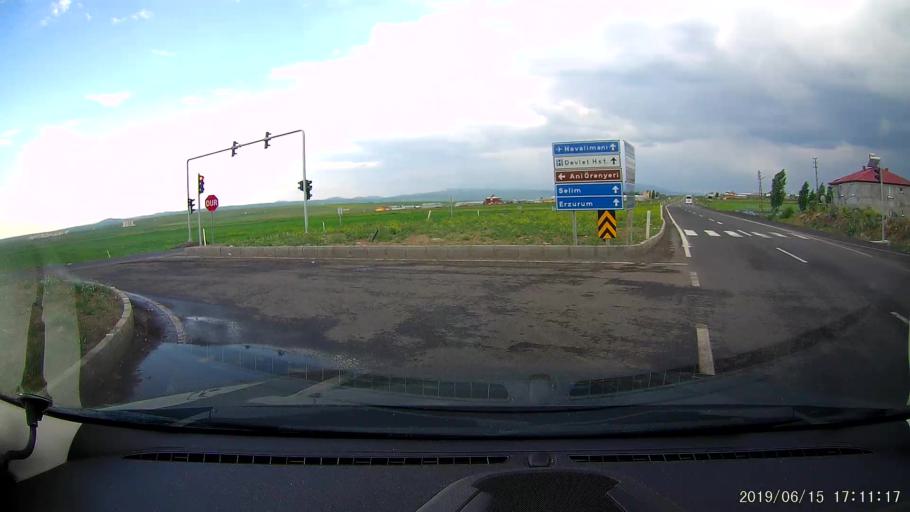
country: TR
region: Kars
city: Kars
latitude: 40.6136
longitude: 43.1333
